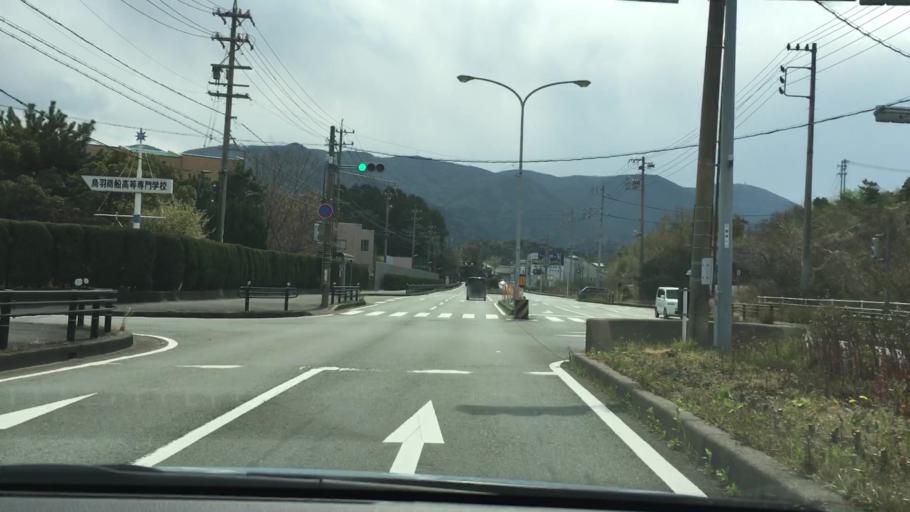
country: JP
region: Mie
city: Toba
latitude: 34.4836
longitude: 136.8250
